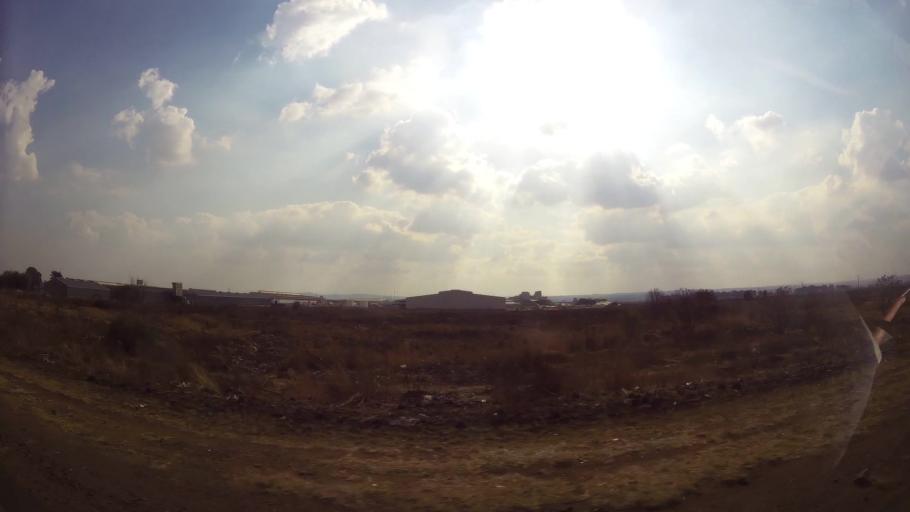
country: ZA
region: Gauteng
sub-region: Ekurhuleni Metropolitan Municipality
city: Germiston
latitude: -26.3088
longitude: 28.2063
